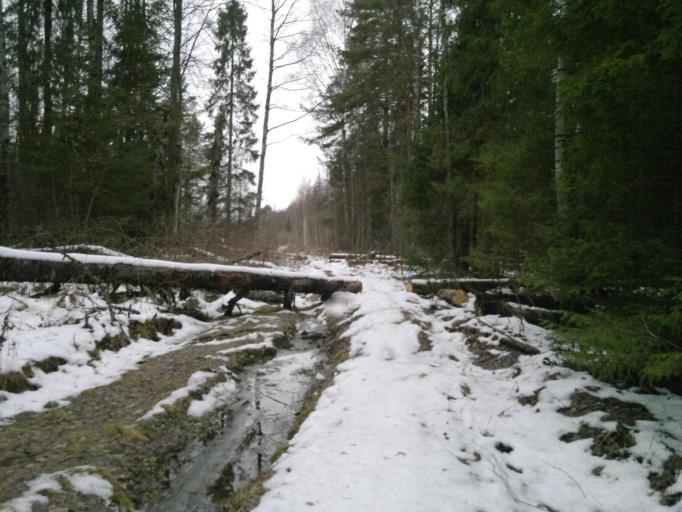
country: RU
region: Mariy-El
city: Yoshkar-Ola
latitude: 56.6038
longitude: 47.9592
